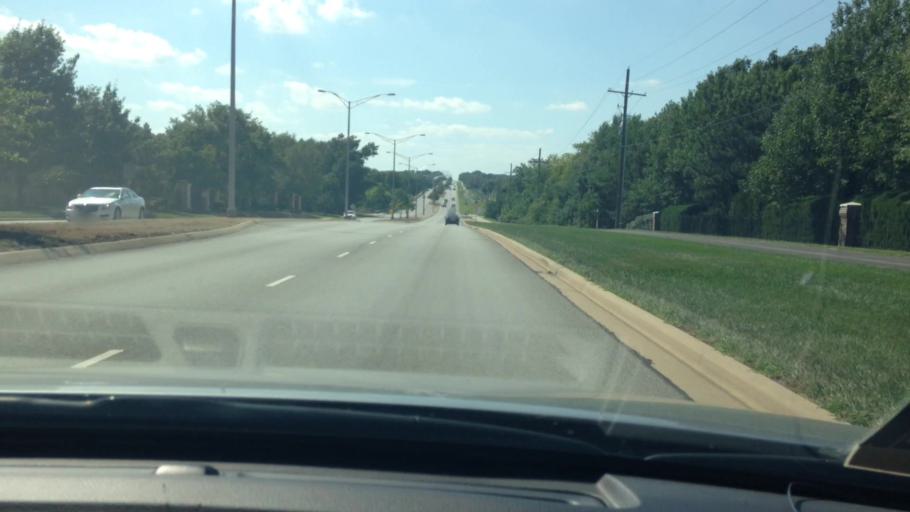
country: US
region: Kansas
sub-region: Johnson County
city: Lenexa
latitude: 38.8692
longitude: -94.6906
